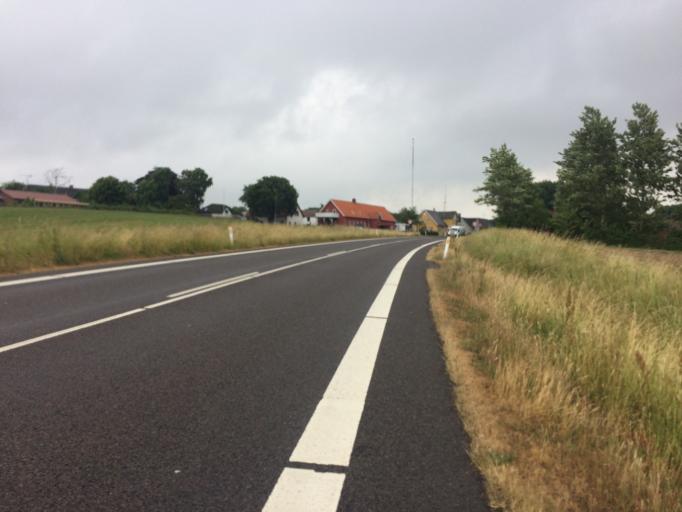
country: DK
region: Capital Region
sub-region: Bornholm Kommune
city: Akirkeby
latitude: 55.1437
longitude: 14.8673
